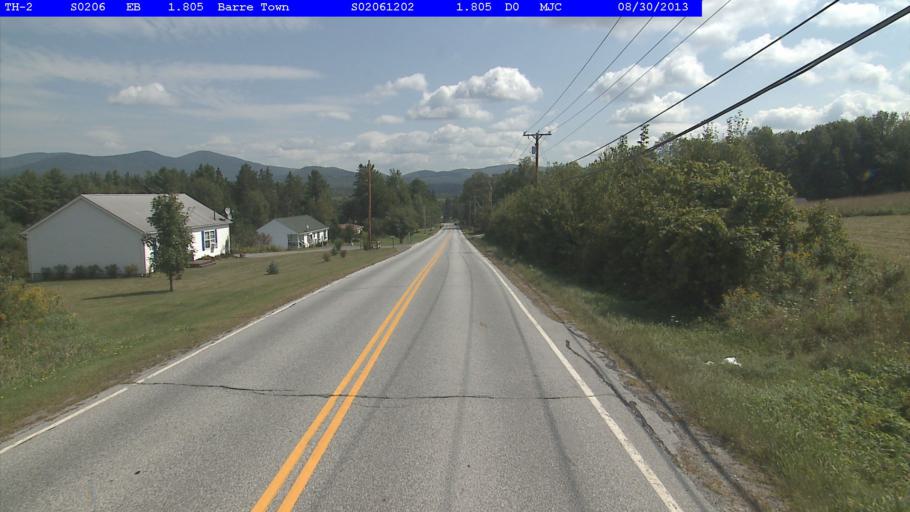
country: US
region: Vermont
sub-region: Washington County
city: South Barre
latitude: 44.1602
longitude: -72.4613
